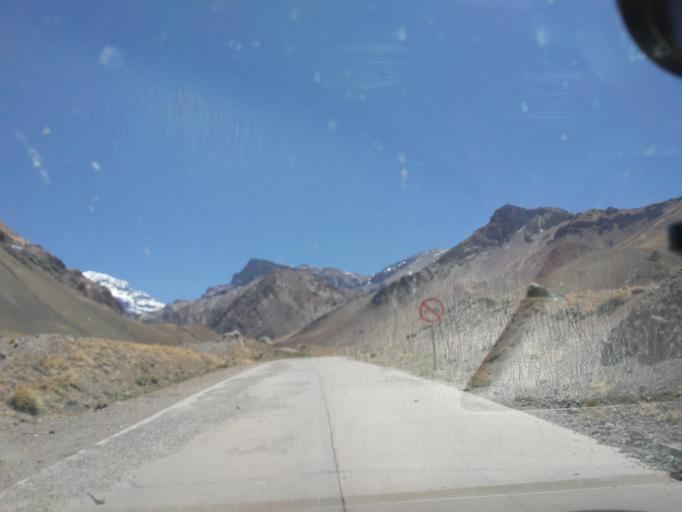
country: CL
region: Valparaiso
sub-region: Provincia de Los Andes
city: Los Andes
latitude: -32.8227
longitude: -69.9422
